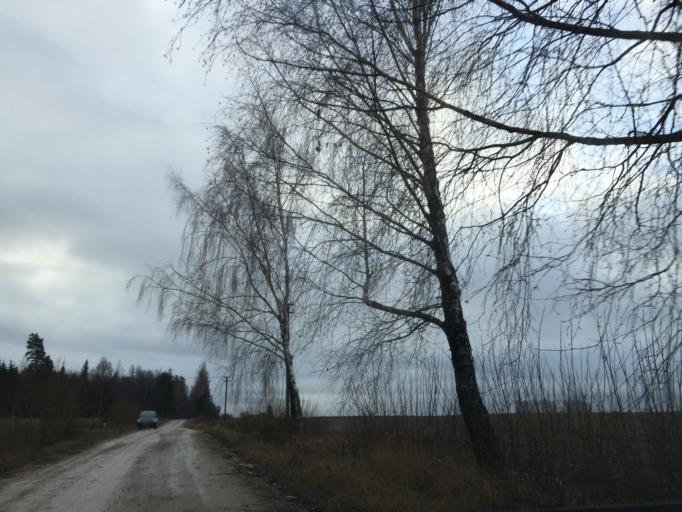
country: LV
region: Vainode
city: Vainode
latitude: 56.6085
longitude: 21.7983
